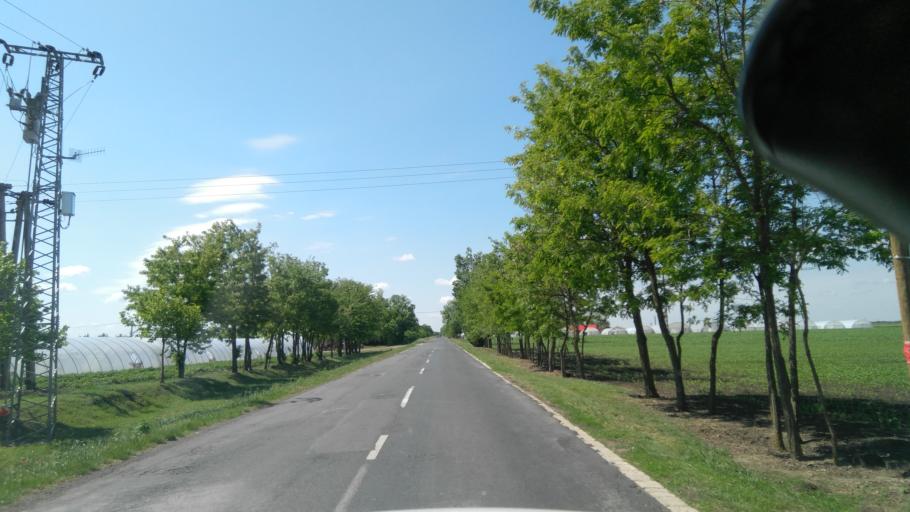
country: HU
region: Bekes
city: Medgyesegyhaza
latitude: 46.4865
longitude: 21.0247
